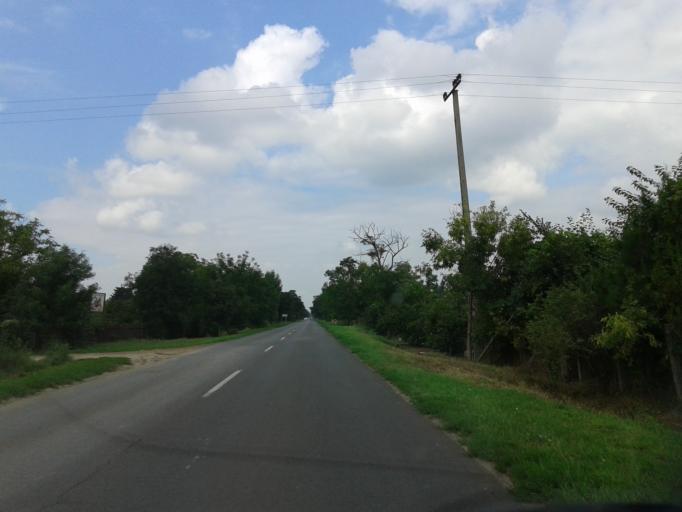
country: HU
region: Csongrad
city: Domaszek
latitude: 46.2761
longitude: 20.0207
